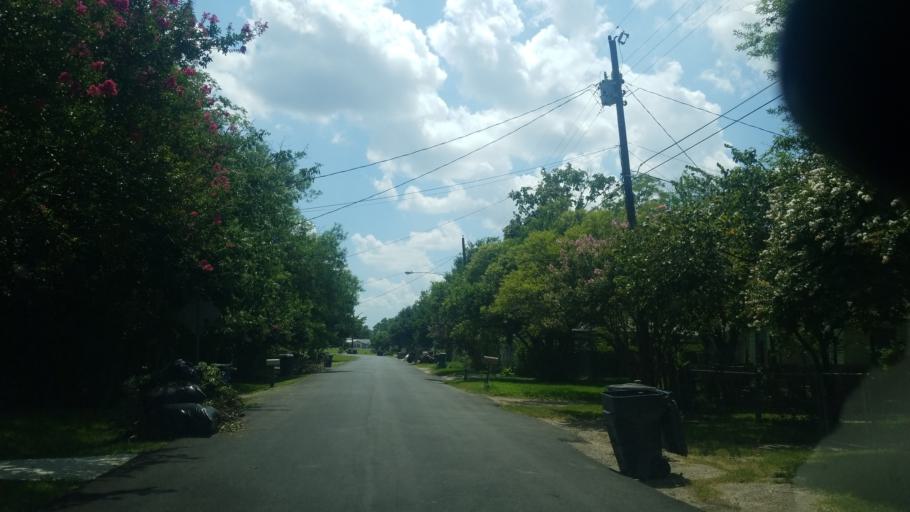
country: US
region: Texas
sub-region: Dallas County
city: Dallas
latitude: 32.7174
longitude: -96.7690
